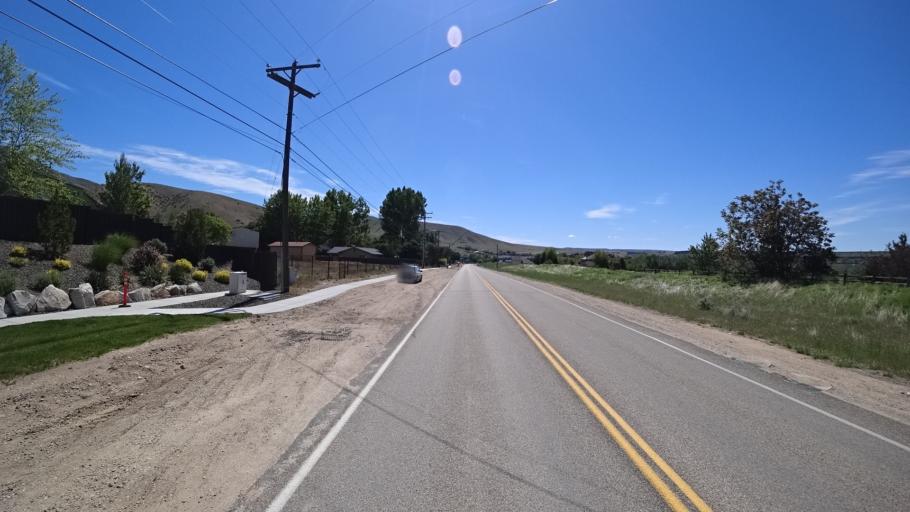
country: US
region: Idaho
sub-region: Ada County
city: Boise
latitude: 43.5604
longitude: -116.1030
